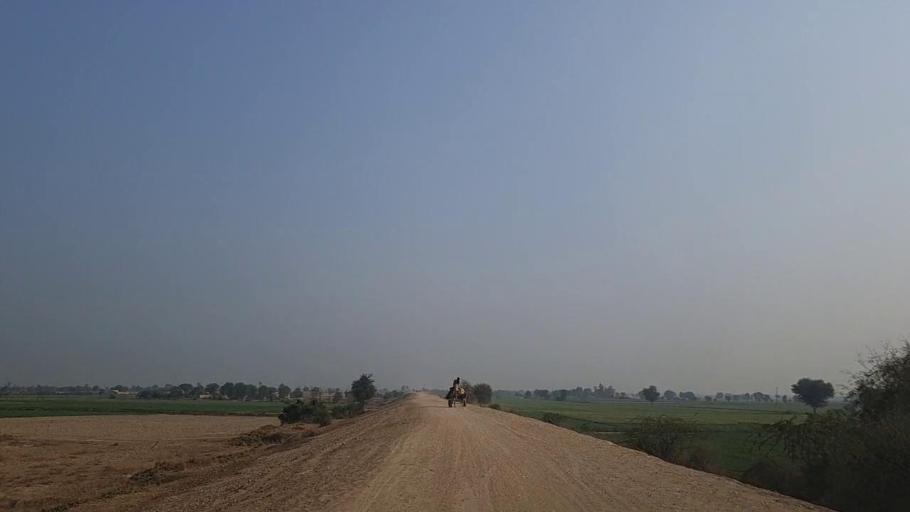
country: PK
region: Sindh
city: Sann
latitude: 26.0933
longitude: 68.1481
